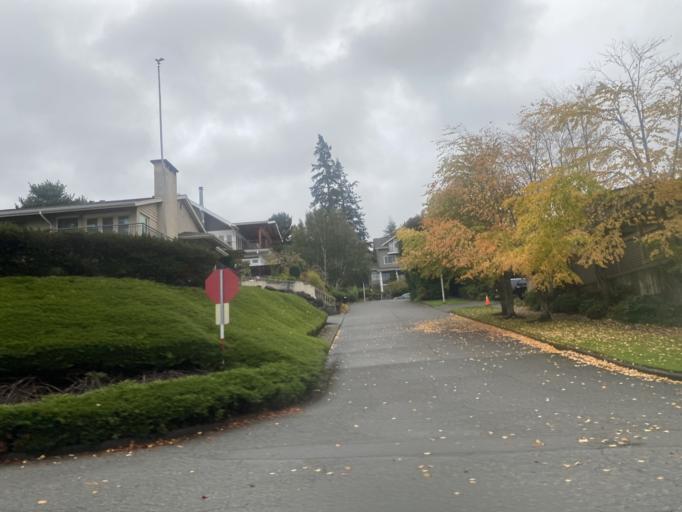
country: US
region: Washington
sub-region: King County
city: Seattle
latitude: 47.6469
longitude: -122.4143
